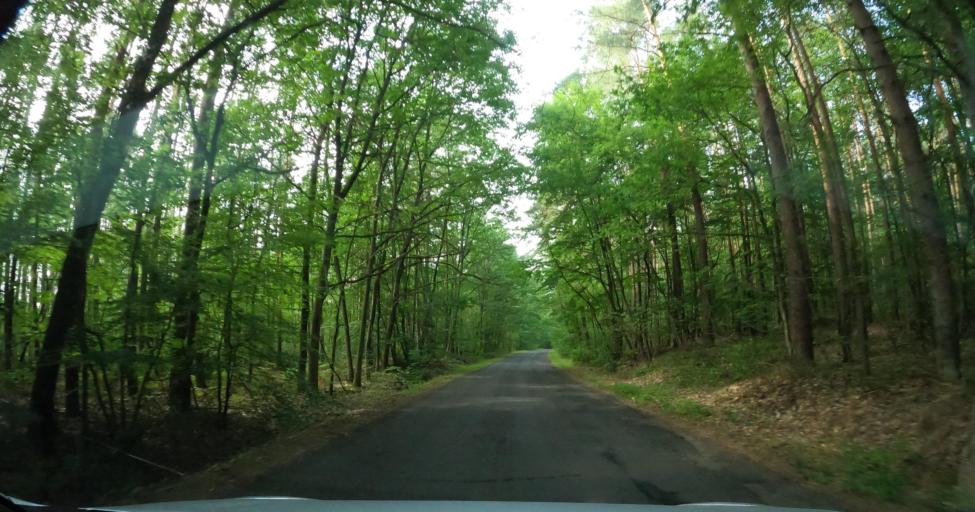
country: PL
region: West Pomeranian Voivodeship
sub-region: Powiat goleniowski
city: Goleniow
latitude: 53.5170
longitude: 14.8580
